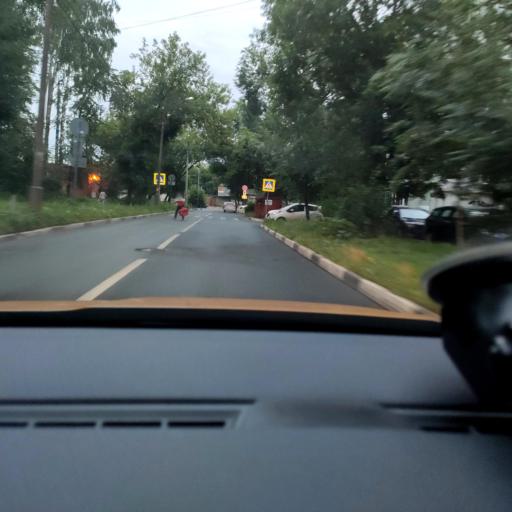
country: RU
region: Moskovskaya
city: Druzhba
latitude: 55.9154
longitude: 37.7767
